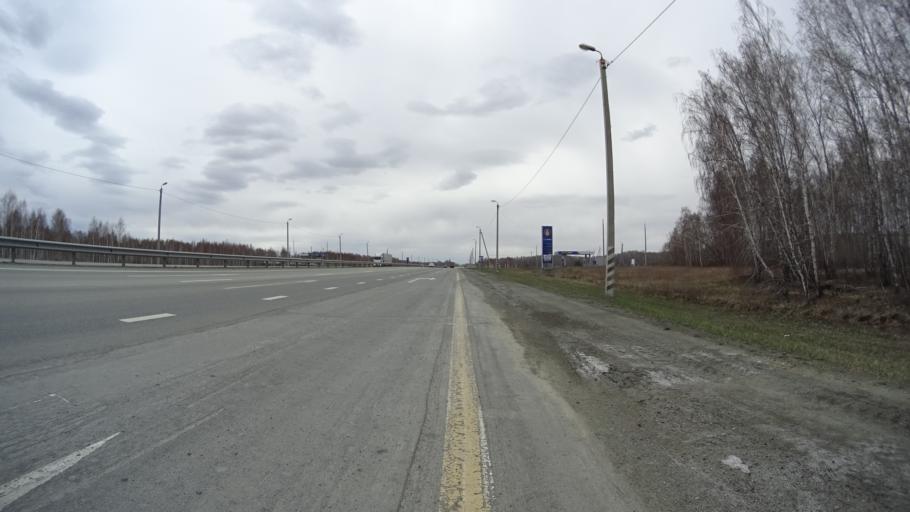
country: RU
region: Chelyabinsk
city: Yemanzhelinka
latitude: 54.8353
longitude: 61.3125
